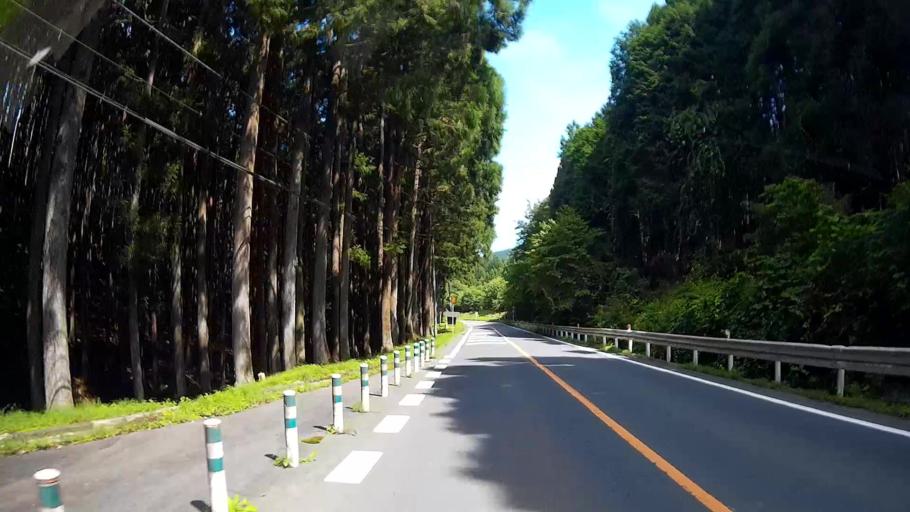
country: JP
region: Saitama
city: Chichibu
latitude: 35.9328
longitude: 139.1528
